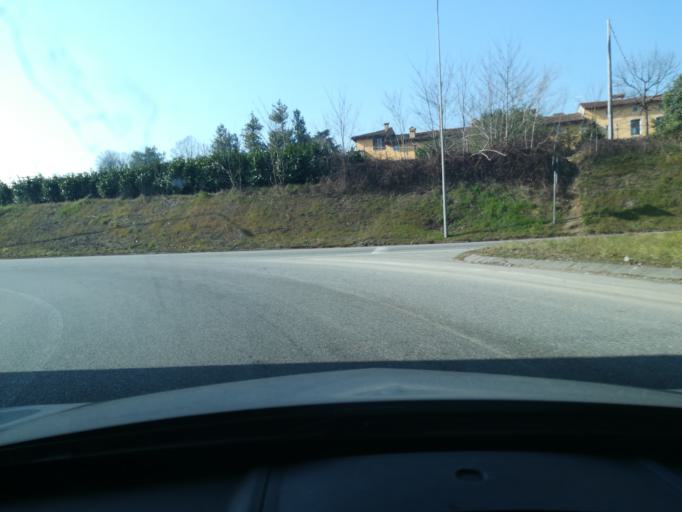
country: IT
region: Lombardy
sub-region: Provincia di Bergamo
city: Grassobbio
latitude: 45.6497
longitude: 9.7054
